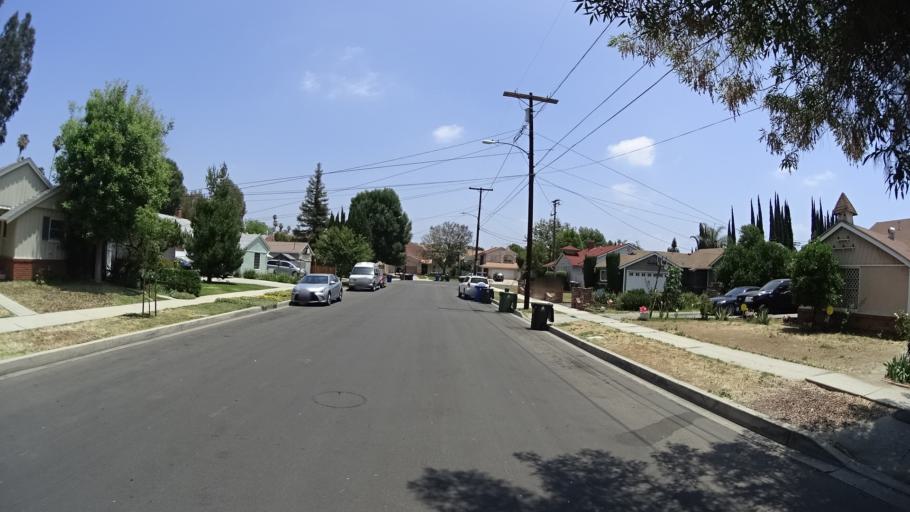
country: US
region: California
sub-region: Los Angeles County
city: Van Nuys
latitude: 34.2001
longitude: -118.4632
